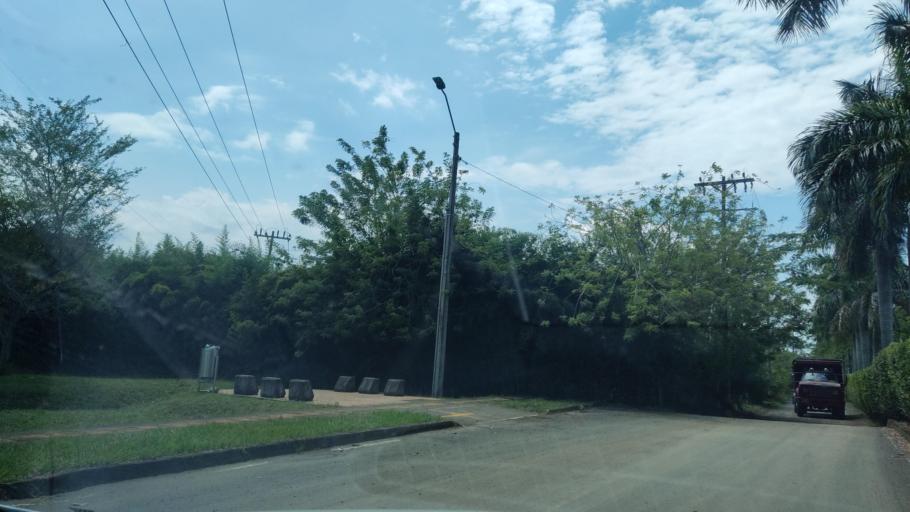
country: CO
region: Valle del Cauca
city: Jamundi
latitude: 3.3012
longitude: -76.5538
